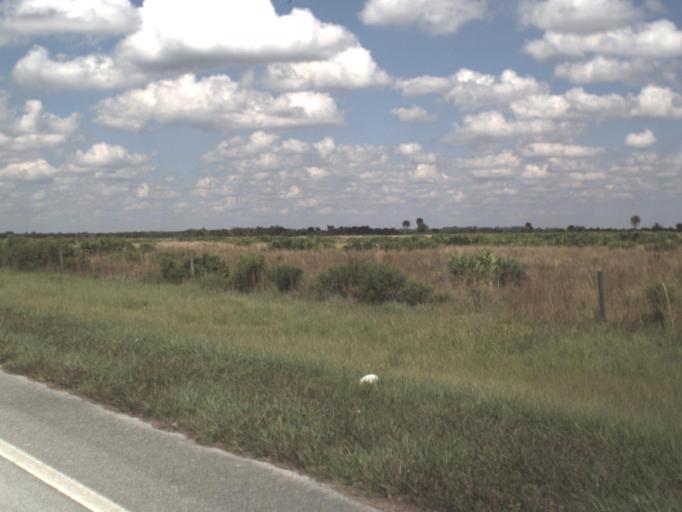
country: US
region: Florida
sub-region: Highlands County
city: Lake Placid
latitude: 27.4261
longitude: -81.2160
